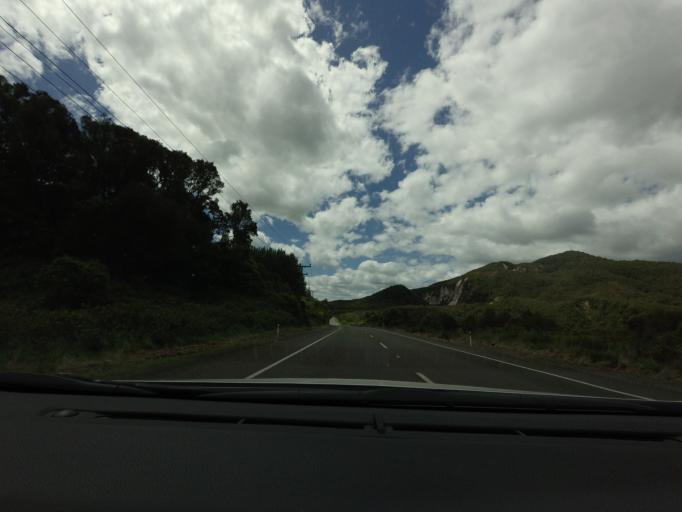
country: NZ
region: Bay of Plenty
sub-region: Rotorua District
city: Rotorua
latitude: -38.3240
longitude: 176.3710
